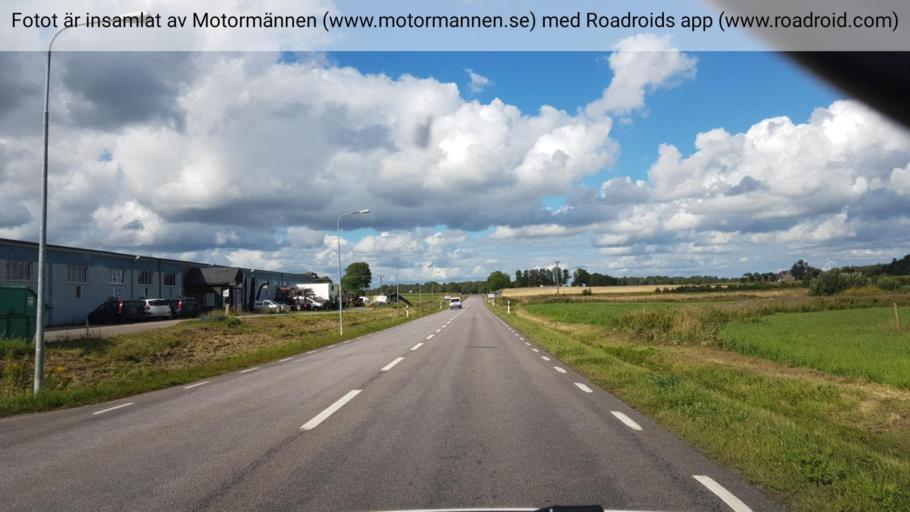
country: SE
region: Vaestra Goetaland
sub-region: Falkopings Kommun
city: Falkoeping
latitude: 58.0876
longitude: 13.5234
